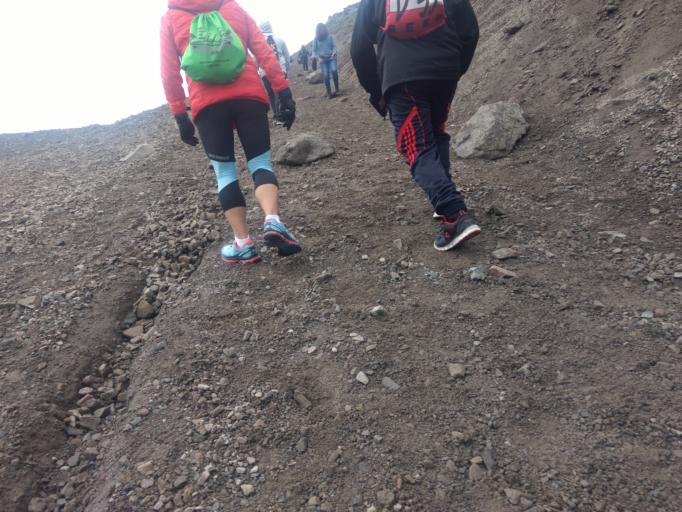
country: MX
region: Mexico
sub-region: Tenango del Valle
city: Santa Cruz Pueblo Nuevo (Pueblo Nuevo)
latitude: 19.1112
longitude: -99.7525
